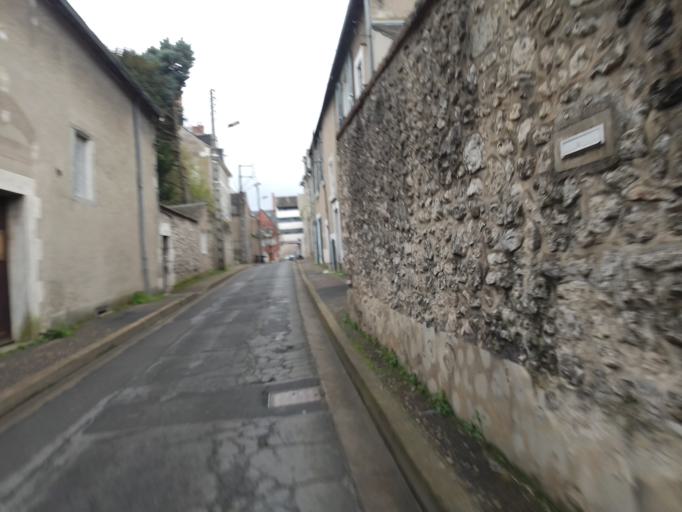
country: FR
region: Centre
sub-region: Departement du Loir-et-Cher
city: Blois
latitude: 47.5902
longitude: 1.3376
